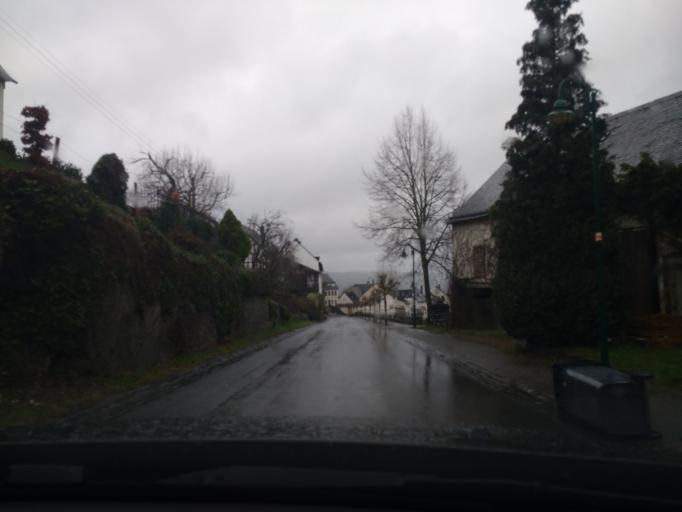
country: DE
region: Rheinland-Pfalz
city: Starkenburg
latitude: 49.9565
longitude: 7.1400
